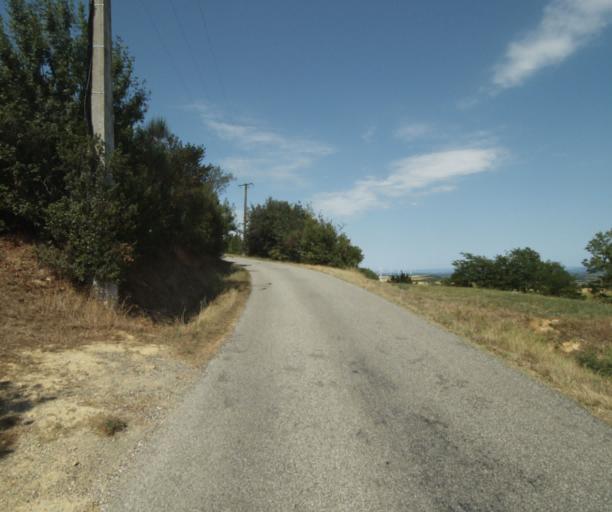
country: FR
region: Midi-Pyrenees
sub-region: Departement de la Haute-Garonne
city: Saint-Felix-Lauragais
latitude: 43.4471
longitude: 1.8897
